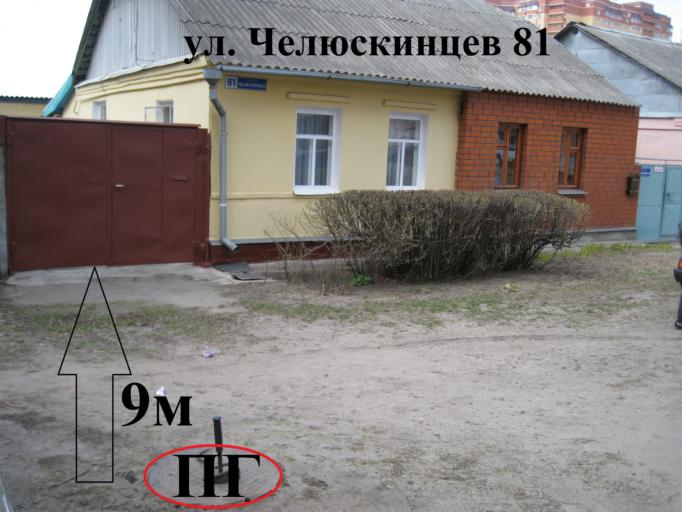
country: RU
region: Voronezj
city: Voronezh
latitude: 51.6474
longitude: 39.1939
